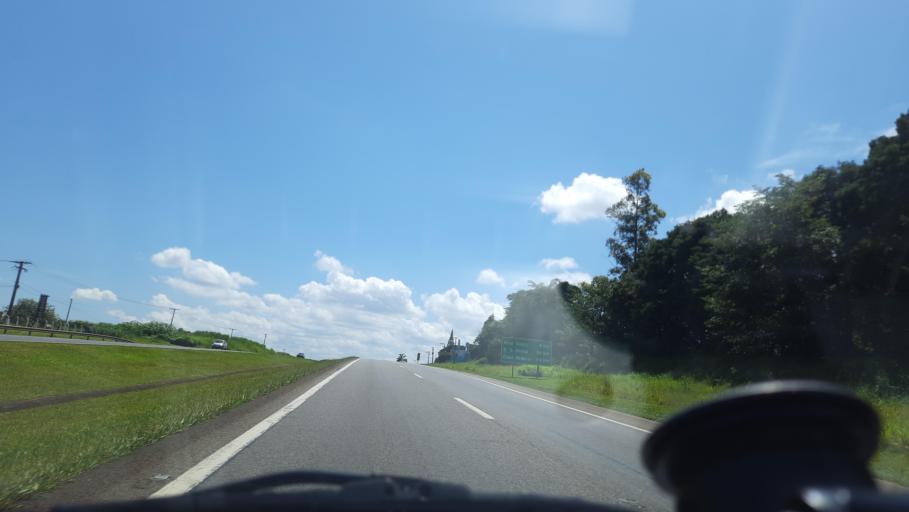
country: BR
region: Sao Paulo
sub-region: Mogi-Mirim
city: Mogi Mirim
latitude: -22.4282
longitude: -46.9829
